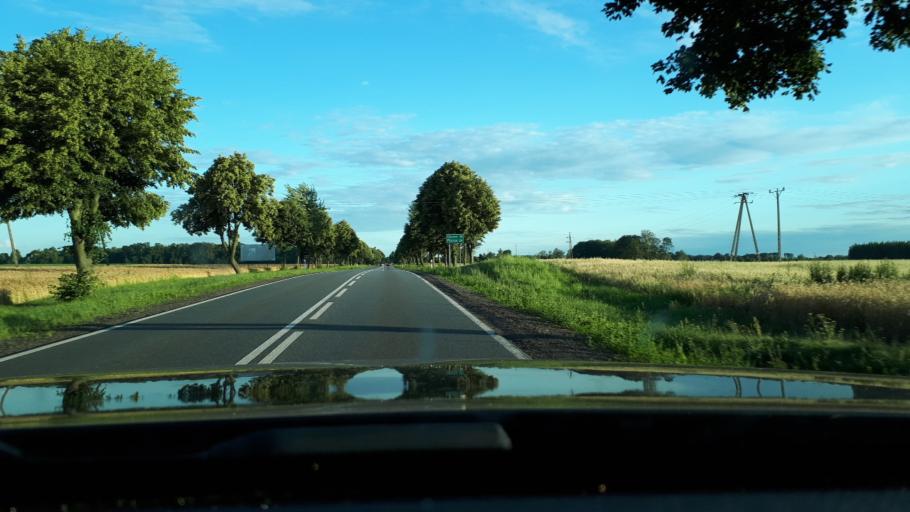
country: PL
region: Masovian Voivodeship
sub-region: Powiat ciechanowski
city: Ciechanow
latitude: 52.8405
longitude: 20.6203
